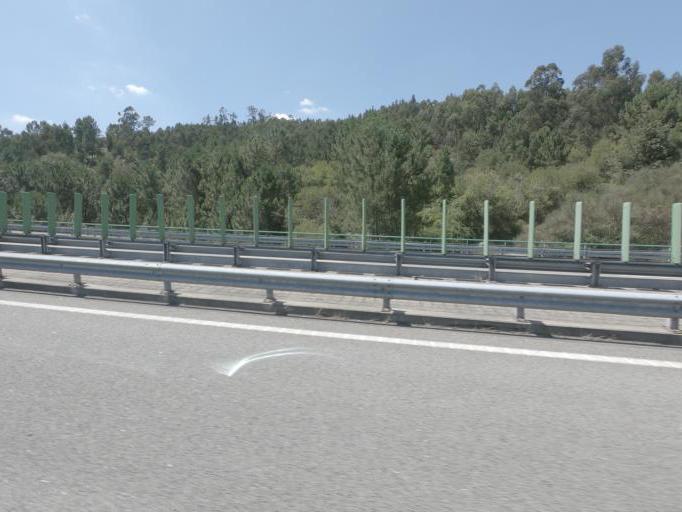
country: PT
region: Porto
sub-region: Amarante
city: Amarante
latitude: 41.2353
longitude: -8.1211
